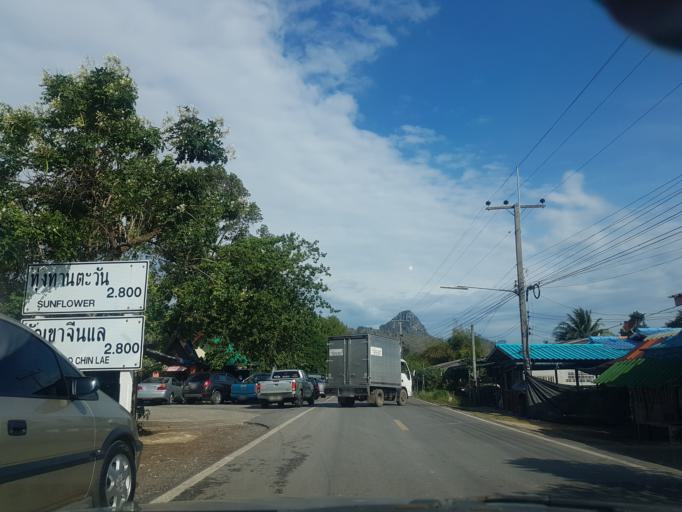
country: TH
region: Sara Buri
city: Phra Phutthabat
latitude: 14.8046
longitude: 100.7526
